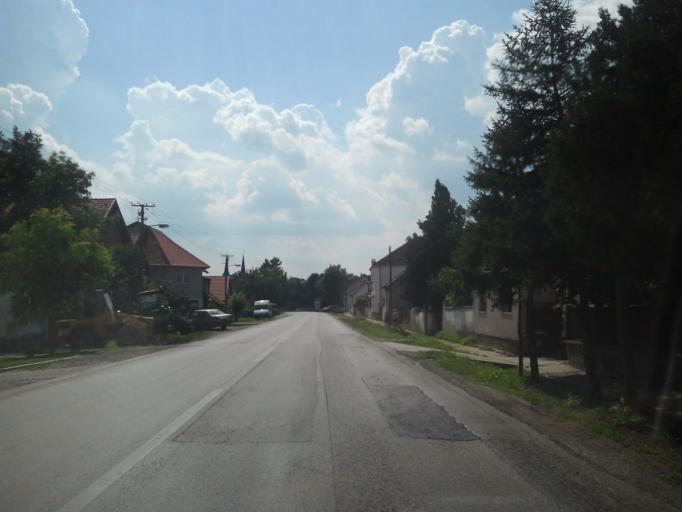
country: RS
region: Autonomna Pokrajina Vojvodina
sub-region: Juznobacki Okrug
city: Beocin
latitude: 45.2402
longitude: 19.7053
